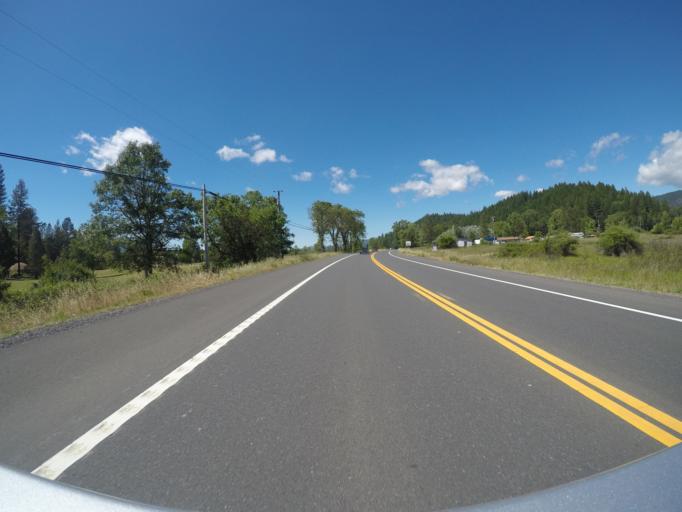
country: US
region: California
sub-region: Mendocino County
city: Laytonville
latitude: 39.6478
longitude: -123.4763
